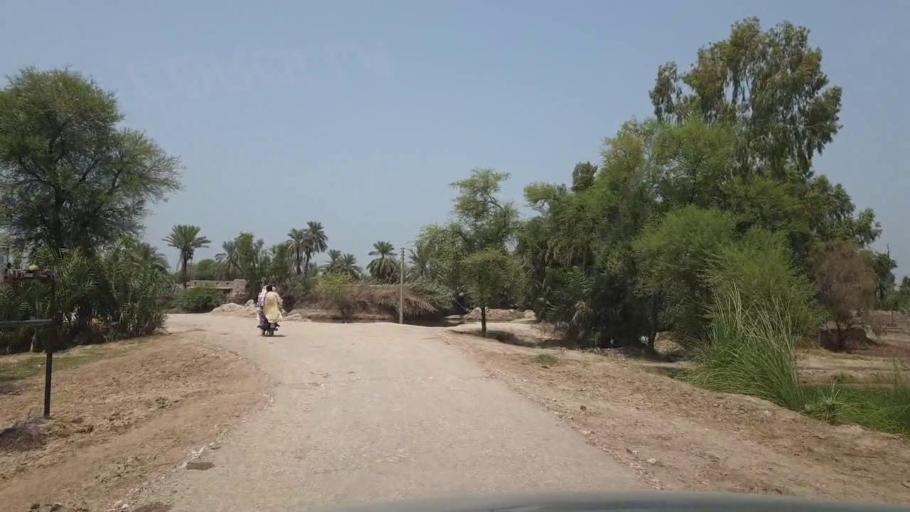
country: PK
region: Sindh
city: Garhi Yasin
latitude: 27.8697
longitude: 68.4555
